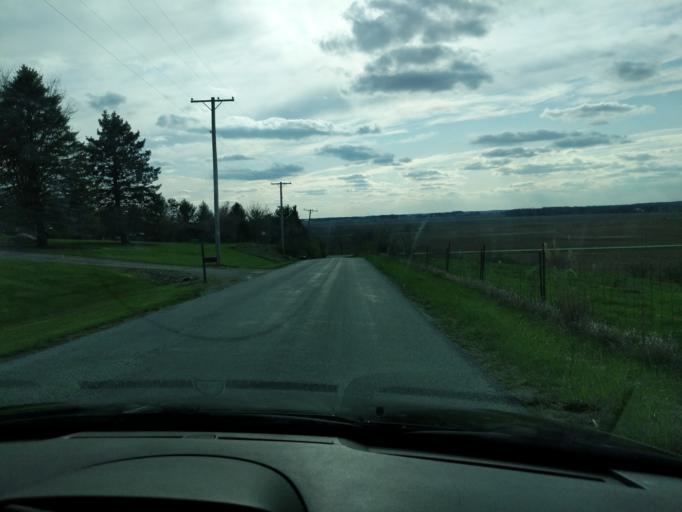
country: US
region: Ohio
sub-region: Champaign County
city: Urbana
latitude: 40.1287
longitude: -83.6715
